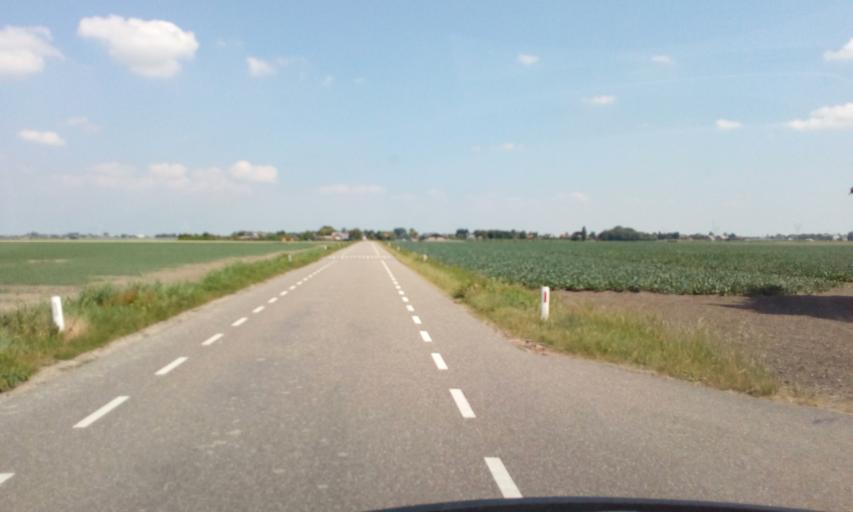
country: NL
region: South Holland
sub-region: Gemeente Rijnwoude
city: Benthuizen
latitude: 52.0857
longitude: 4.5557
